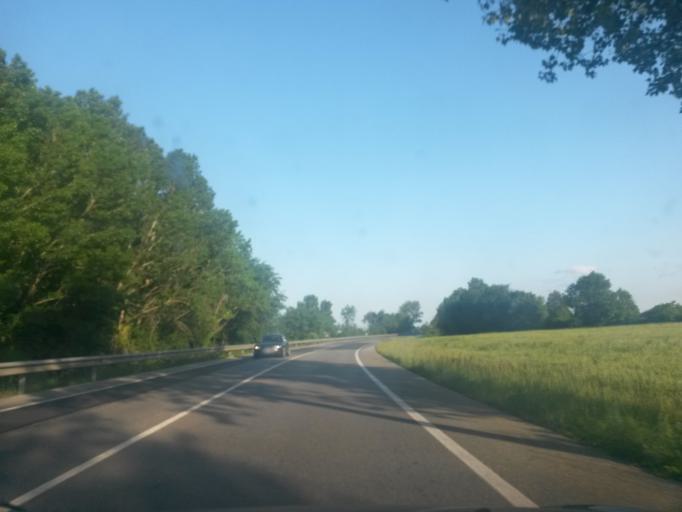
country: ES
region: Catalonia
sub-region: Provincia de Girona
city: Banyoles
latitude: 42.1518
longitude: 2.7606
